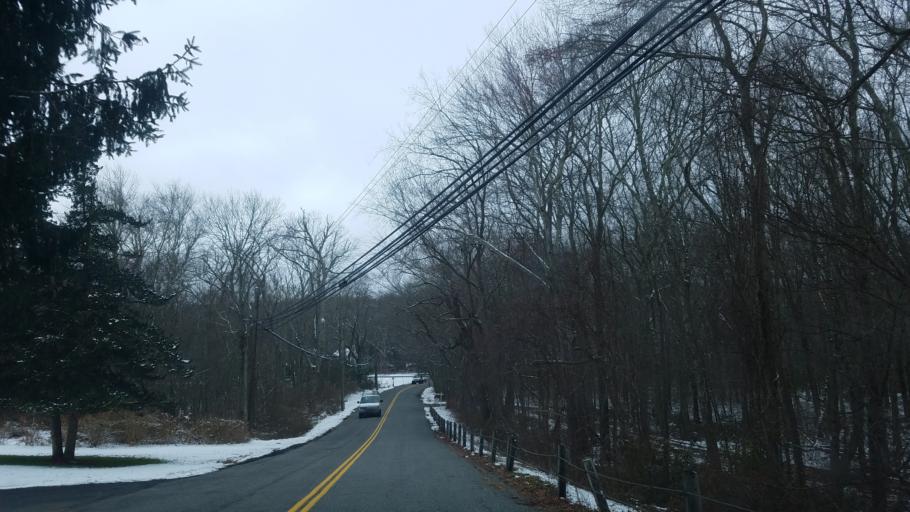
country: US
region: Connecticut
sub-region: New London County
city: Central Waterford
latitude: 41.3939
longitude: -72.1732
